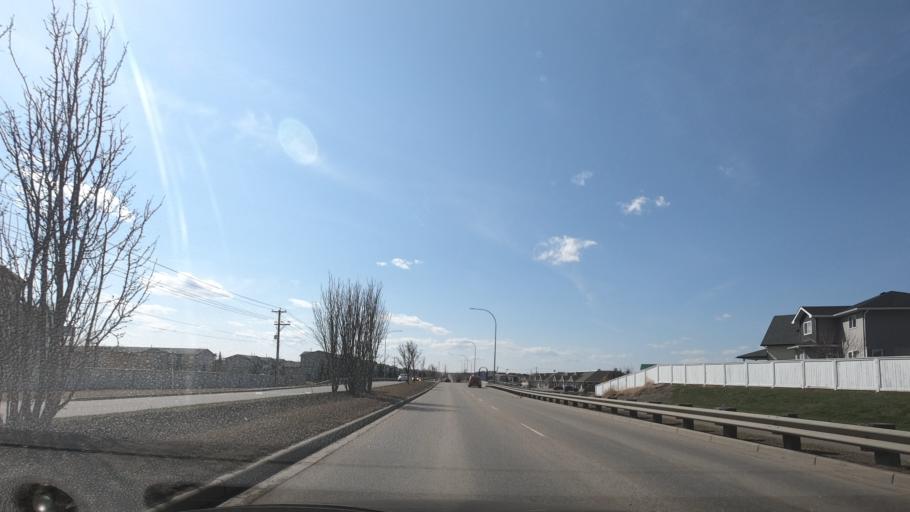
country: CA
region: Alberta
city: Airdrie
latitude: 51.3001
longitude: -114.0209
